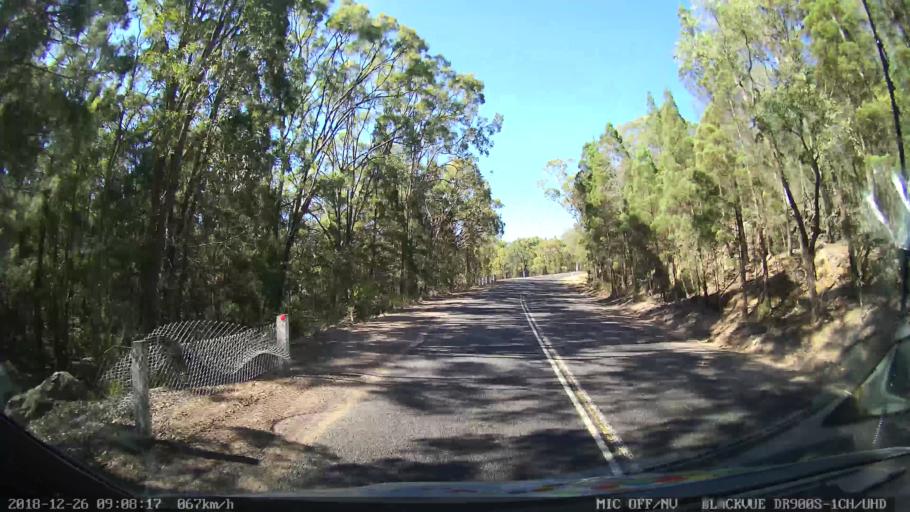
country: AU
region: New South Wales
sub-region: Mid-Western Regional
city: Kandos
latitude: -32.7150
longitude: 150.0031
